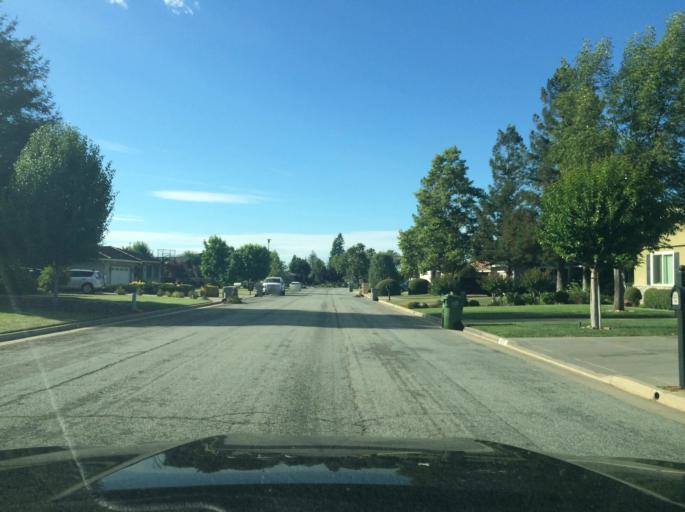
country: US
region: California
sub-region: Santa Clara County
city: Cambrian Park
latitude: 37.2166
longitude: -121.8758
